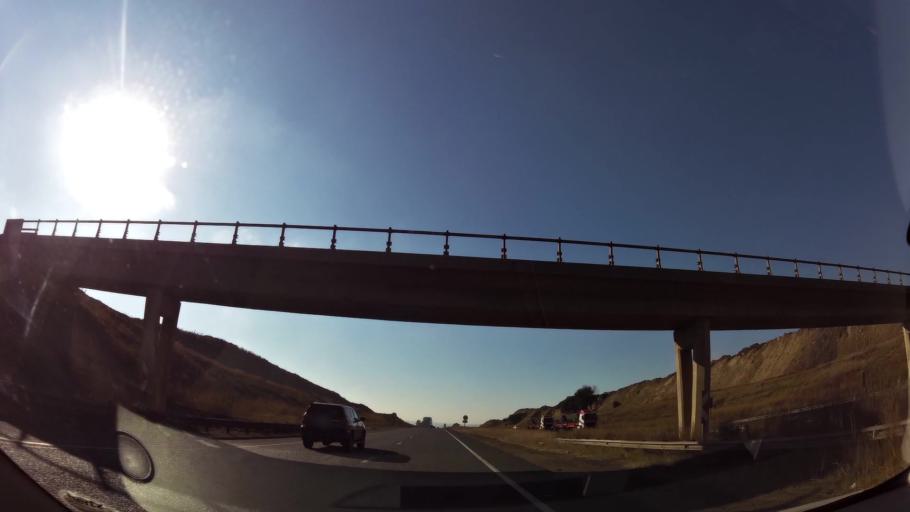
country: ZA
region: Mpumalanga
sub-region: Nkangala District Municipality
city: Witbank
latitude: -26.0176
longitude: 28.9697
